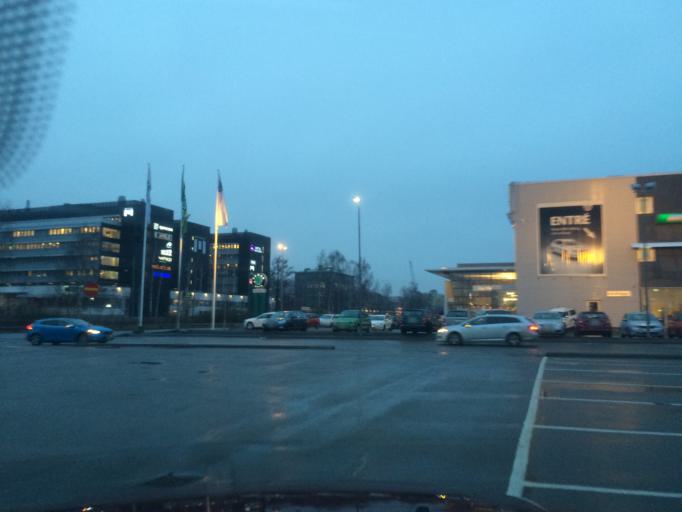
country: SE
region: Vaestra Goetaland
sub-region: Molndal
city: Moelndal
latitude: 57.6806
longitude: 12.0037
